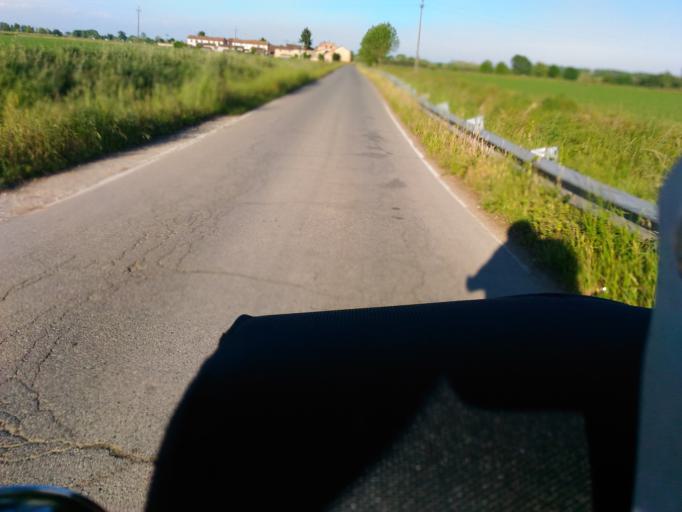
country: IT
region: Lombardy
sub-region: Provincia di Lodi
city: Lodi Vecchio
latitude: 45.2996
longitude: 9.4289
